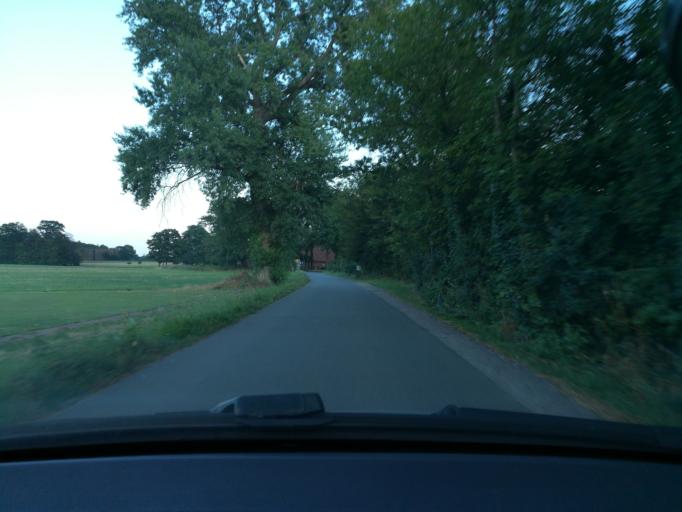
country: DE
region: North Rhine-Westphalia
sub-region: Regierungsbezirk Munster
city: Lienen
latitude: 52.1419
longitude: 7.9870
